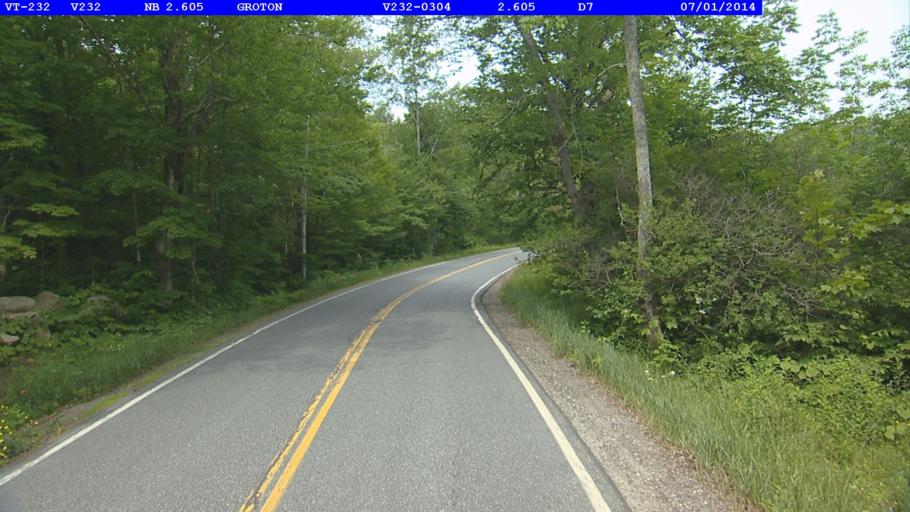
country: US
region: New Hampshire
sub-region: Grafton County
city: Woodsville
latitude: 44.2462
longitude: -72.2554
